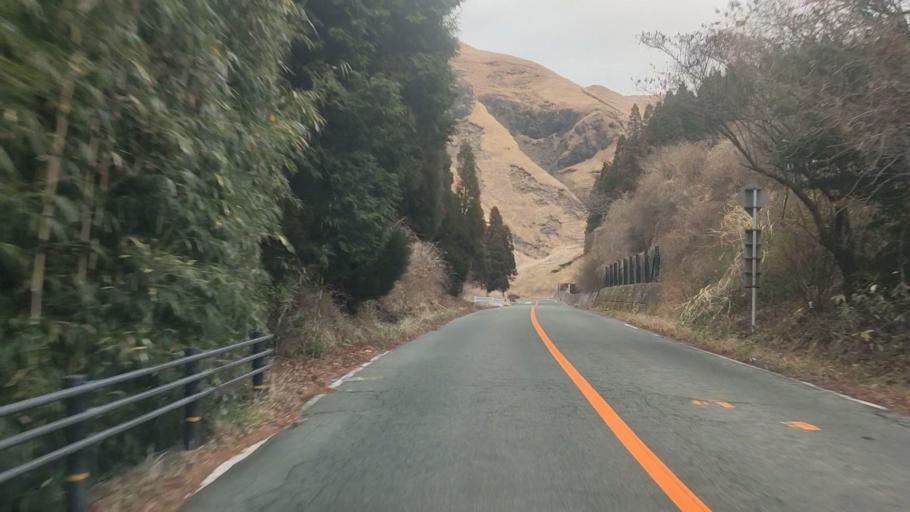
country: JP
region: Kumamoto
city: Aso
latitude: 32.9089
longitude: 131.1430
